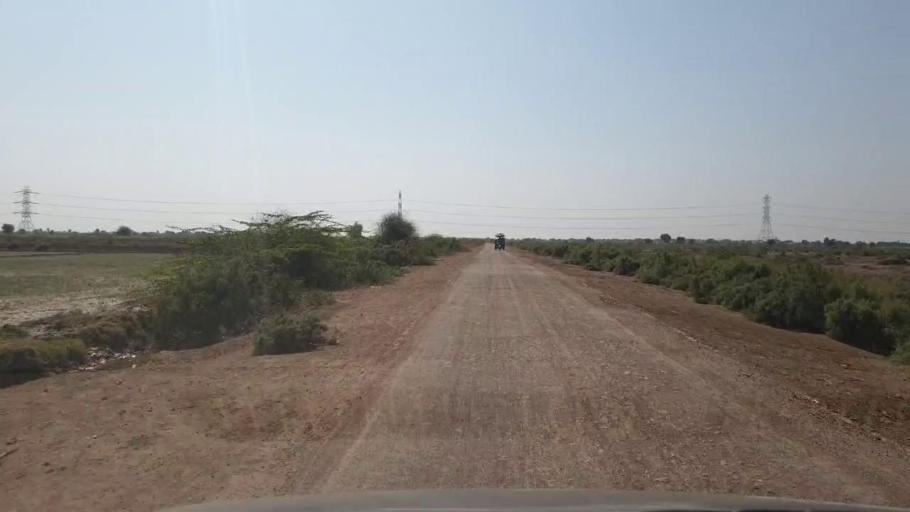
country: PK
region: Sindh
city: Digri
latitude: 25.1910
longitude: 69.2230
